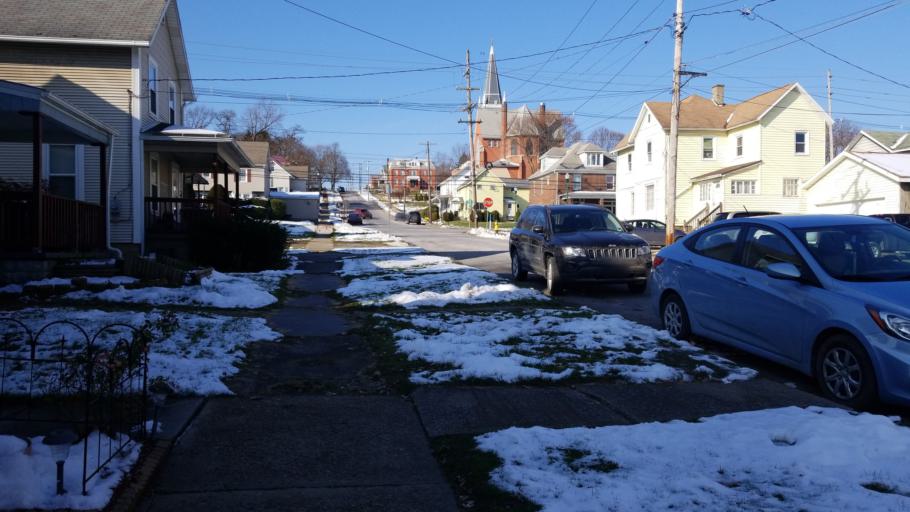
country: US
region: Pennsylvania
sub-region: Clearfield County
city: DuBois
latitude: 41.1192
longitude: -78.7680
